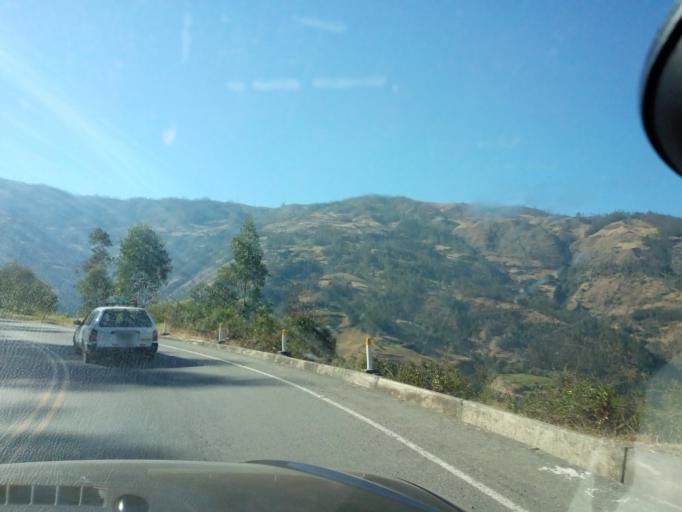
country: PE
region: Apurimac
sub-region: Provincia de Abancay
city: Tamburco
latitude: -13.6184
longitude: -72.8554
